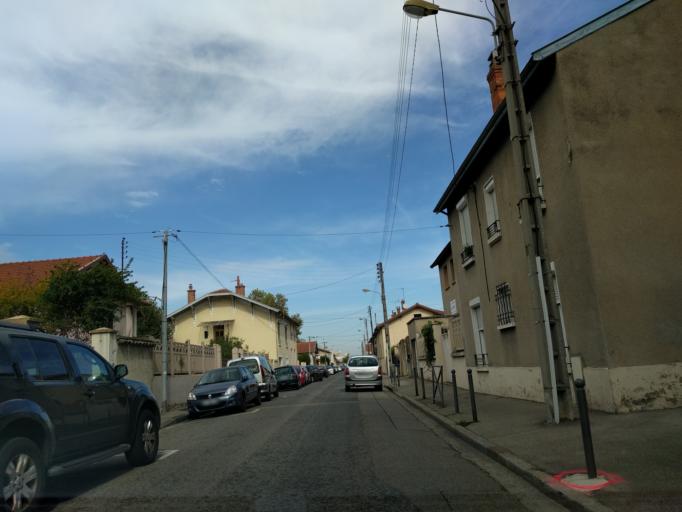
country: FR
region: Rhone-Alpes
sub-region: Departement du Rhone
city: Villeurbanne
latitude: 45.7527
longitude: 4.9025
